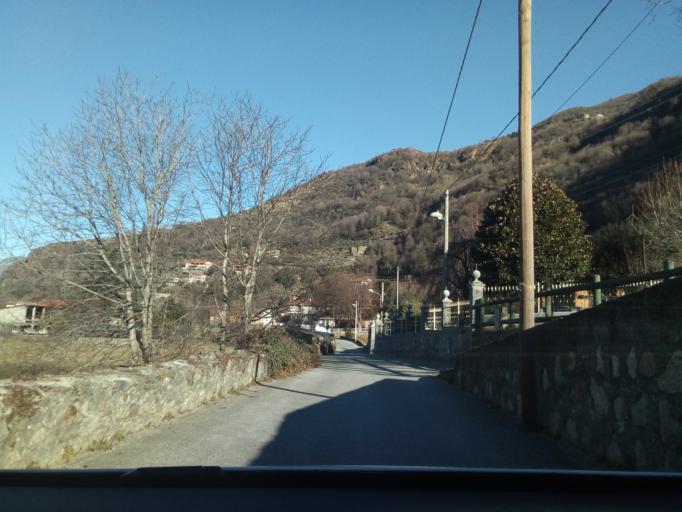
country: IT
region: Piedmont
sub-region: Provincia di Torino
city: Nomaglio
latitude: 45.5313
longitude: 7.8497
